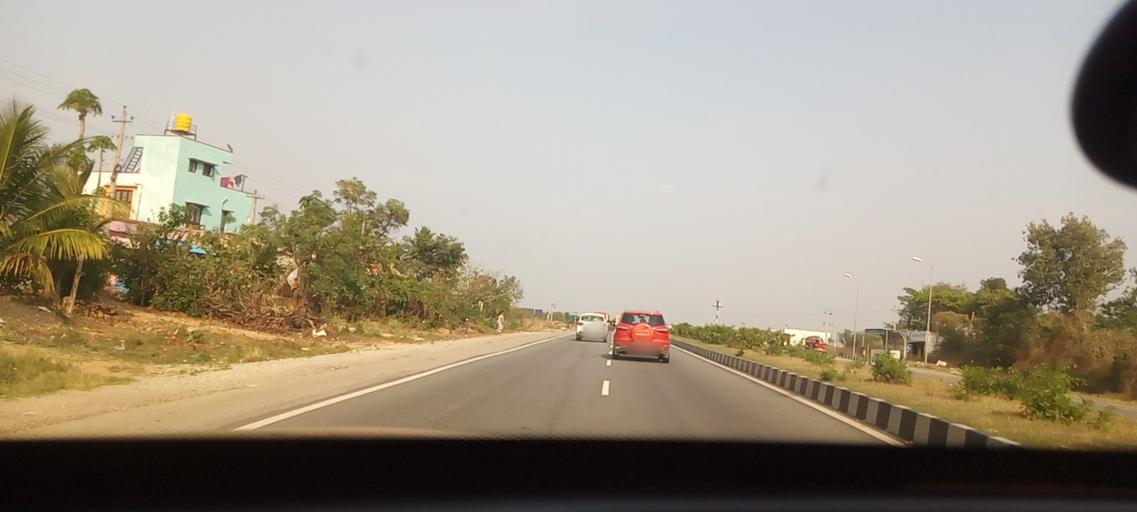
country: IN
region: Karnataka
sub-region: Hassan
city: Channarayapatna
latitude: 12.9763
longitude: 76.3137
